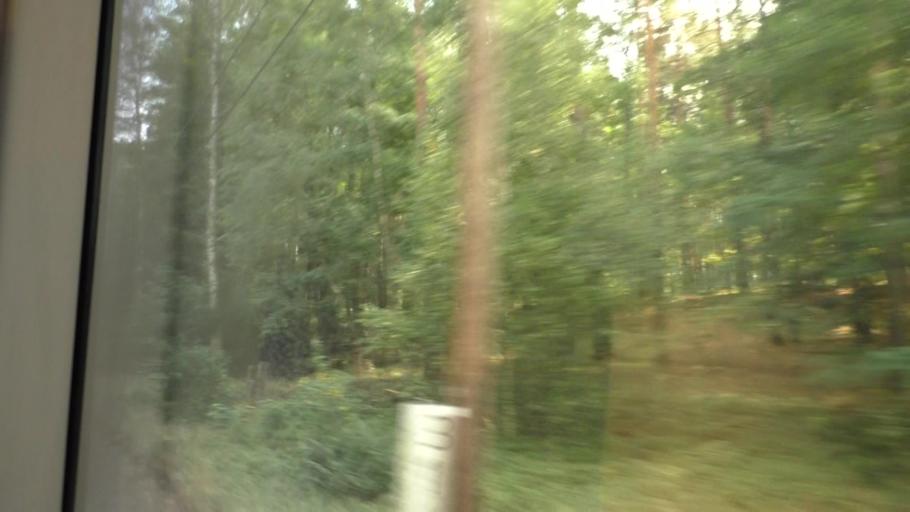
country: DE
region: Brandenburg
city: Wendisch Rietz
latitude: 52.2242
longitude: 13.9780
